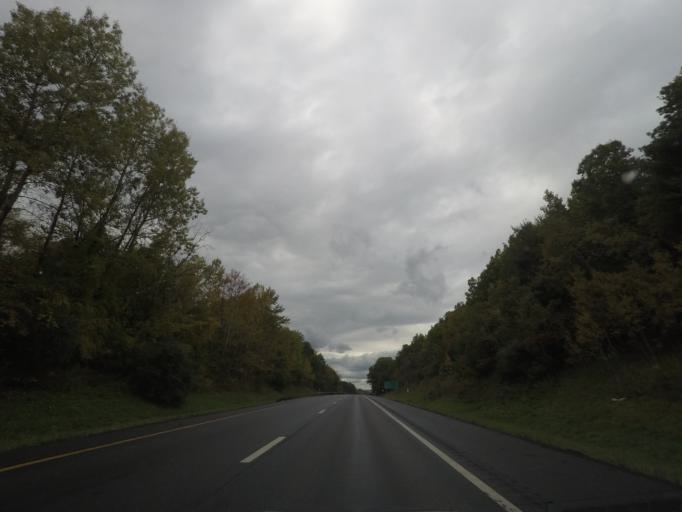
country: US
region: New York
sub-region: Columbia County
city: Niverville
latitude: 42.4846
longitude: -73.6882
